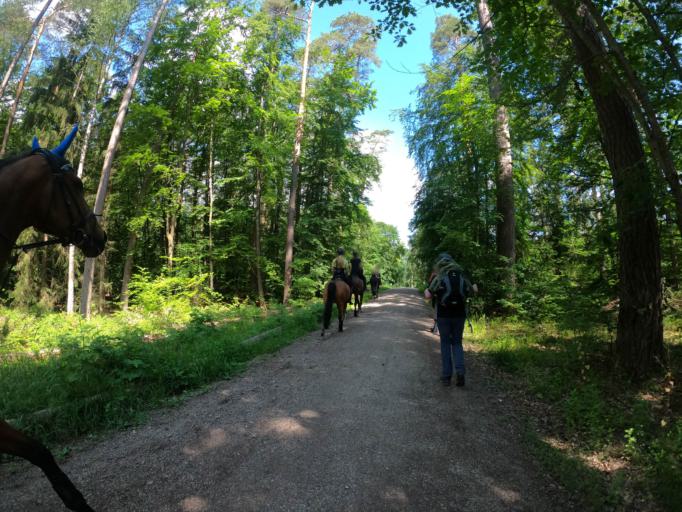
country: DE
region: Bavaria
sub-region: Upper Franconia
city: Memmelsdorf
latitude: 49.8879
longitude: 10.9550
